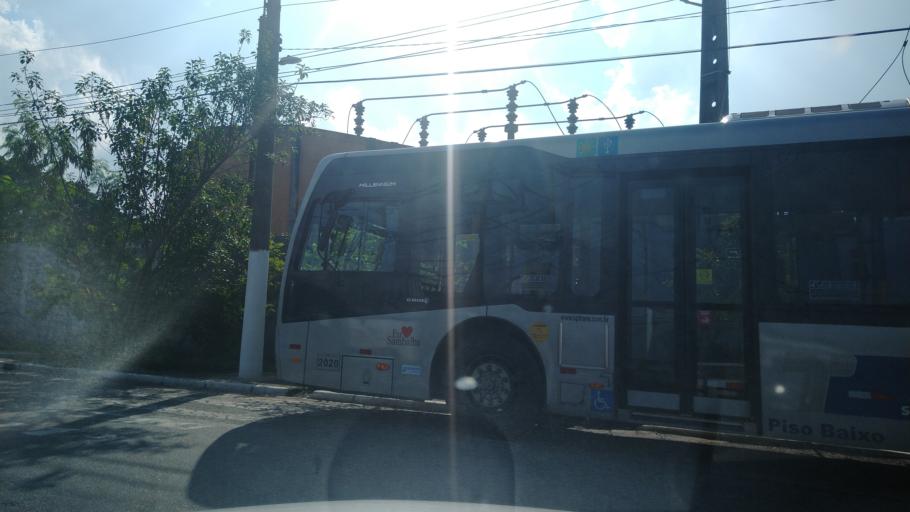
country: BR
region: Sao Paulo
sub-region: Guarulhos
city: Guarulhos
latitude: -23.5123
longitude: -46.5633
